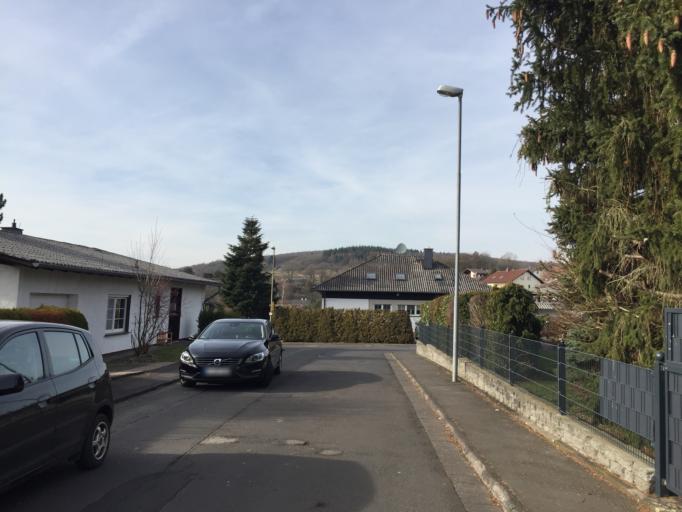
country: DE
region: Hesse
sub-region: Regierungsbezirk Giessen
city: Fronhausen
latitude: 50.6847
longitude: 8.6873
